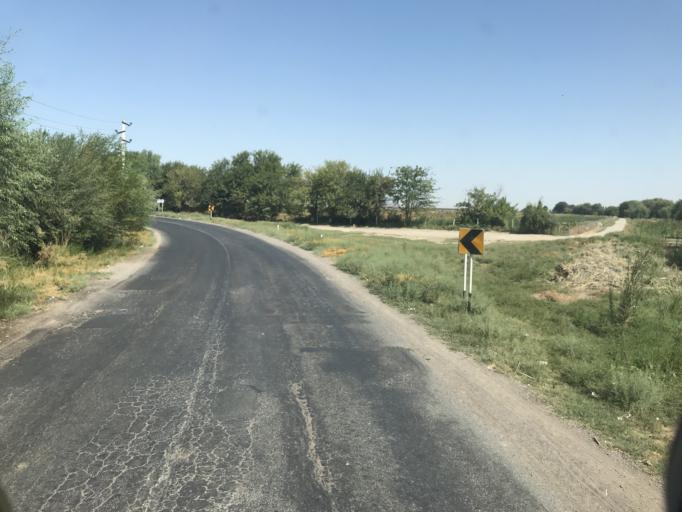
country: KZ
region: Ongtustik Qazaqstan
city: Ilyich
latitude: 40.9479
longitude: 68.4892
